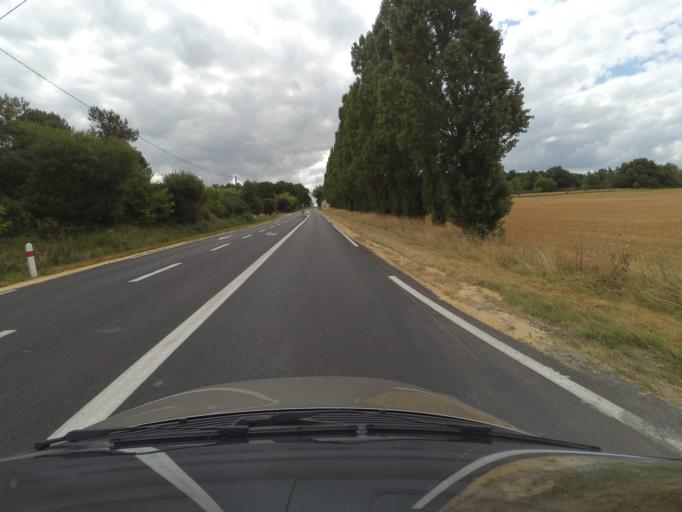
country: FR
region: Poitou-Charentes
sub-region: Departement de la Vienne
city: Saint-Gervais-les-Trois-Clochers
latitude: 46.9088
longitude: 0.4490
